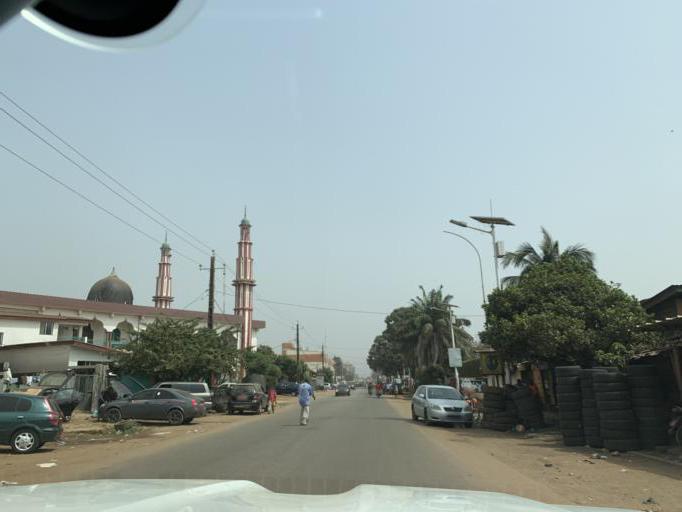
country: GN
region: Conakry
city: Camayenne
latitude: 9.5308
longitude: -13.6815
